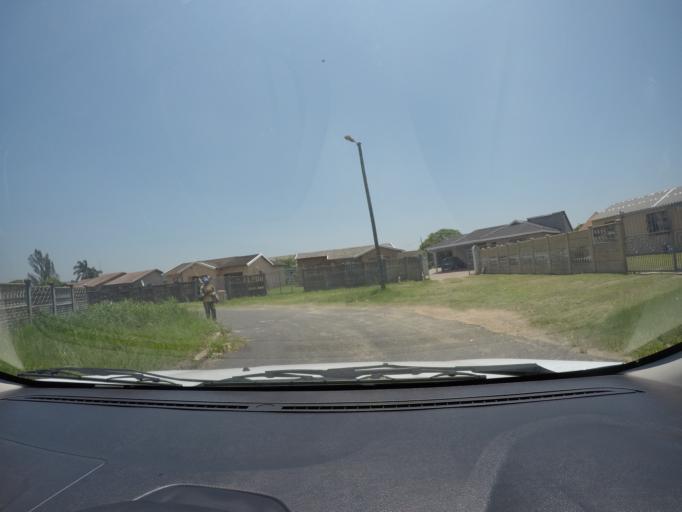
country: ZA
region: KwaZulu-Natal
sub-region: uThungulu District Municipality
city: eSikhawini
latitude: -28.8724
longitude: 31.9038
